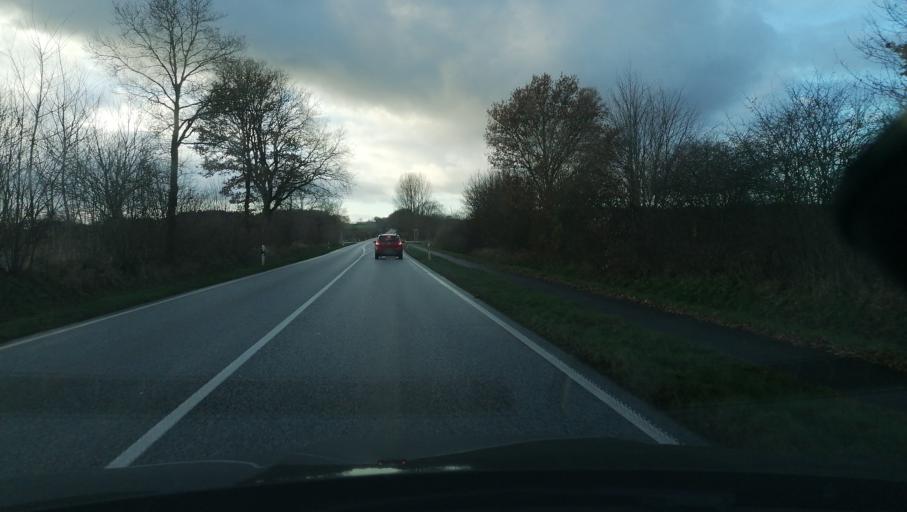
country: DE
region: Schleswig-Holstein
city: Tensbuttel-Rost
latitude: 54.1141
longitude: 9.2462
